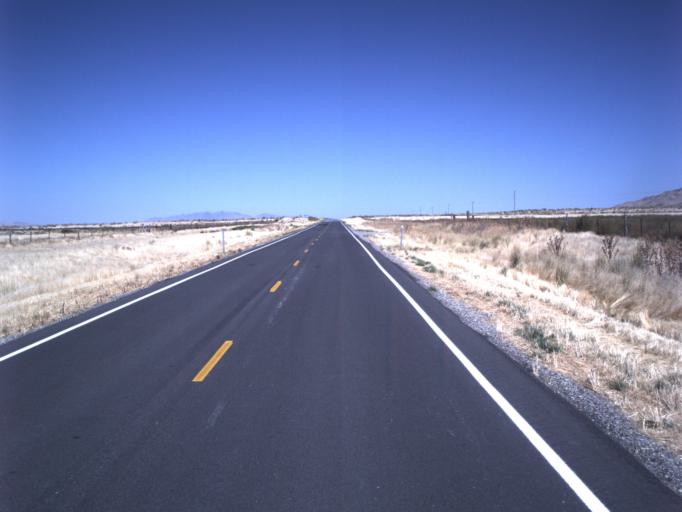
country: US
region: Utah
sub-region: Tooele County
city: Grantsville
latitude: 40.5021
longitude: -112.7480
